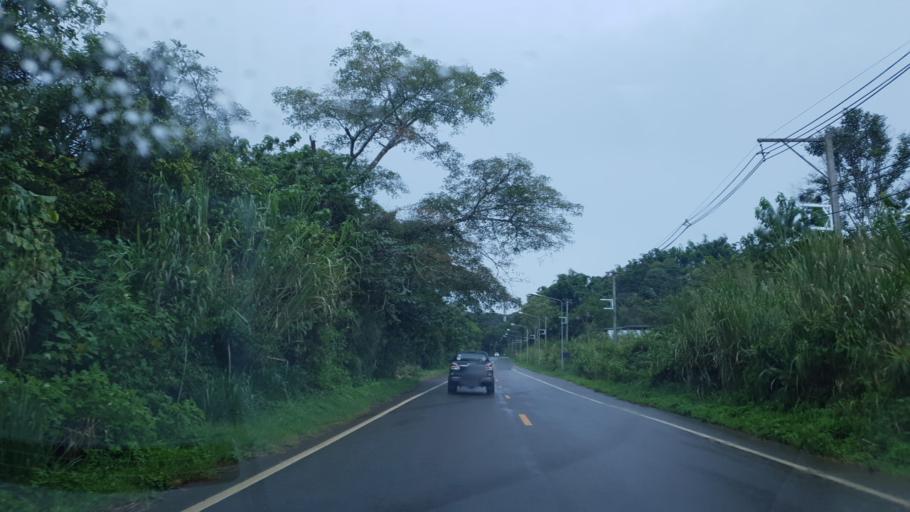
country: TH
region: Mae Hong Son
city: Ban Huai I Huak
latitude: 18.1601
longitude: 98.0672
